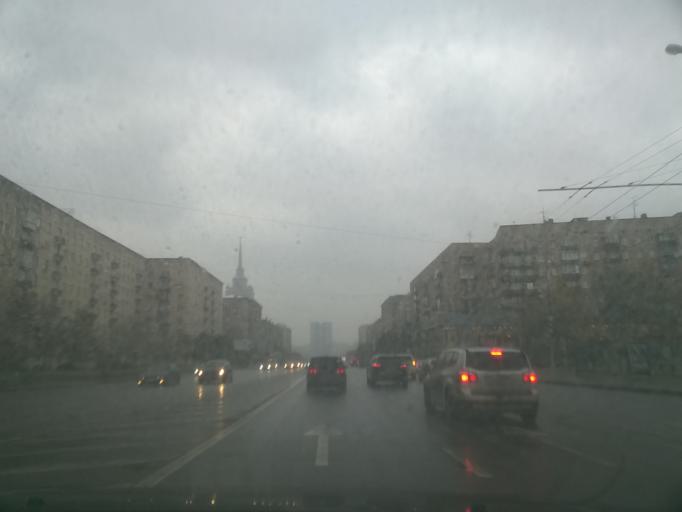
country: RU
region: Moskovskaya
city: Presnenskiy
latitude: 55.7470
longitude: 37.5547
